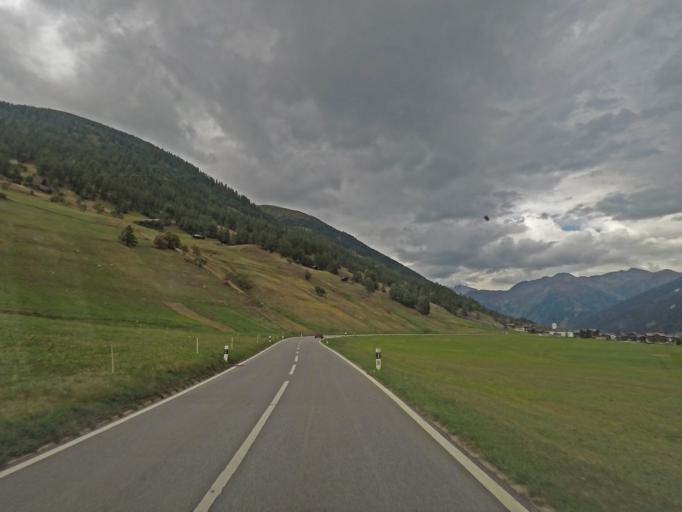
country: IT
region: Piedmont
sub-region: Provincia Verbano-Cusio-Ossola
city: Formazza
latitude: 46.5031
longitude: 8.2962
